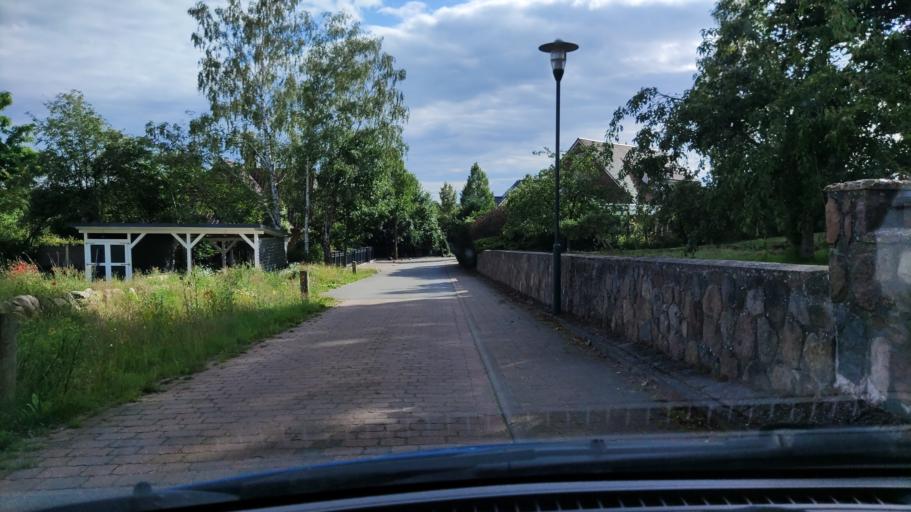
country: DE
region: Lower Saxony
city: Salzhausen
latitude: 53.2253
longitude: 10.1501
